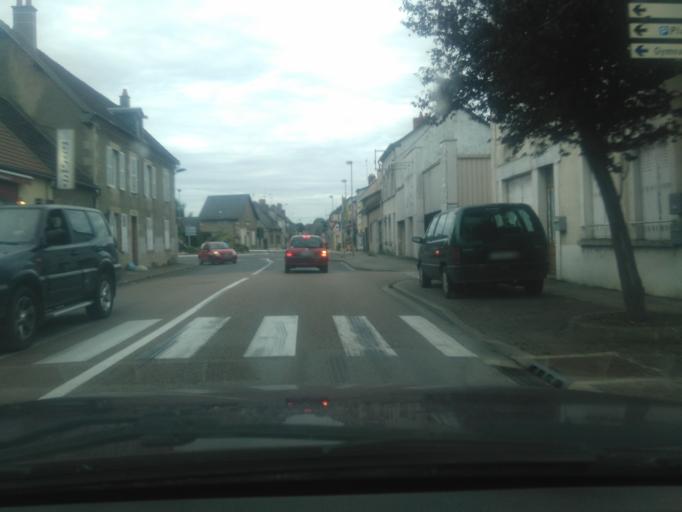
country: FR
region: Bourgogne
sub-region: Departement de la Nievre
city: Decize
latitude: 46.8268
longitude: 3.4542
